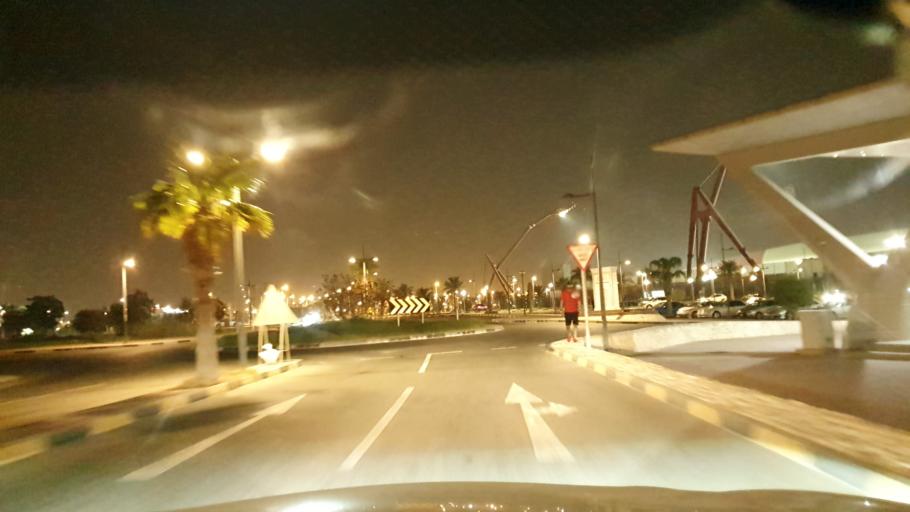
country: BH
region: Northern
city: Madinat `Isa
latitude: 26.1558
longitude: 50.5456
